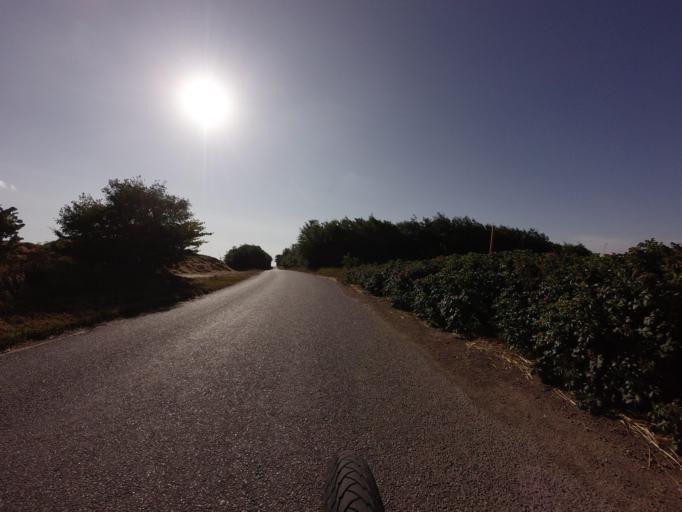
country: DK
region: North Denmark
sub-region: Hjorring Kommune
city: Vra
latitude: 57.3819
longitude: 9.9972
